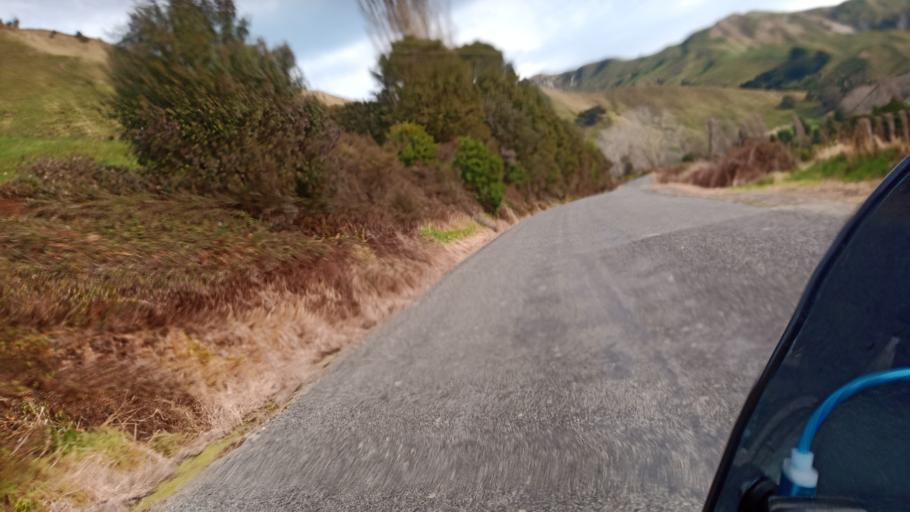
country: NZ
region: Hawke's Bay
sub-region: Wairoa District
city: Wairoa
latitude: -38.7956
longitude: 177.4441
